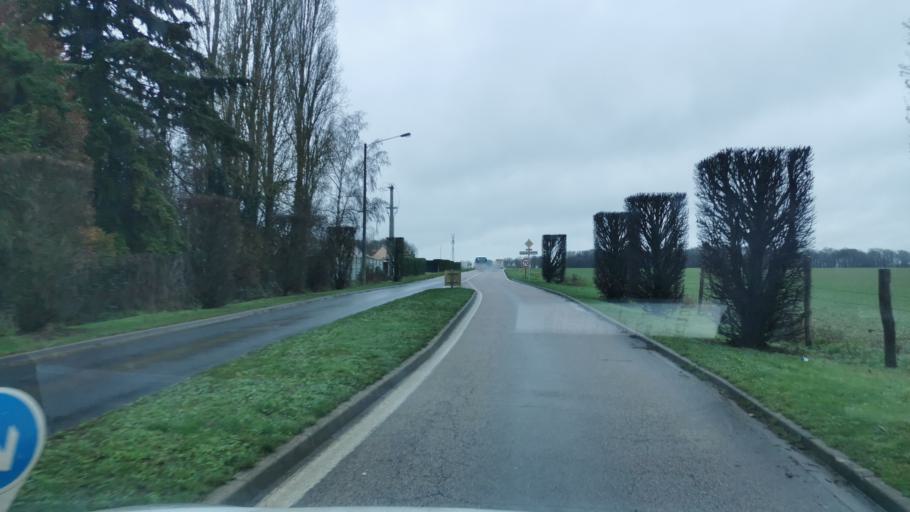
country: FR
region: Haute-Normandie
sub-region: Departement de l'Eure
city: Normanville
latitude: 49.0854
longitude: 1.1799
